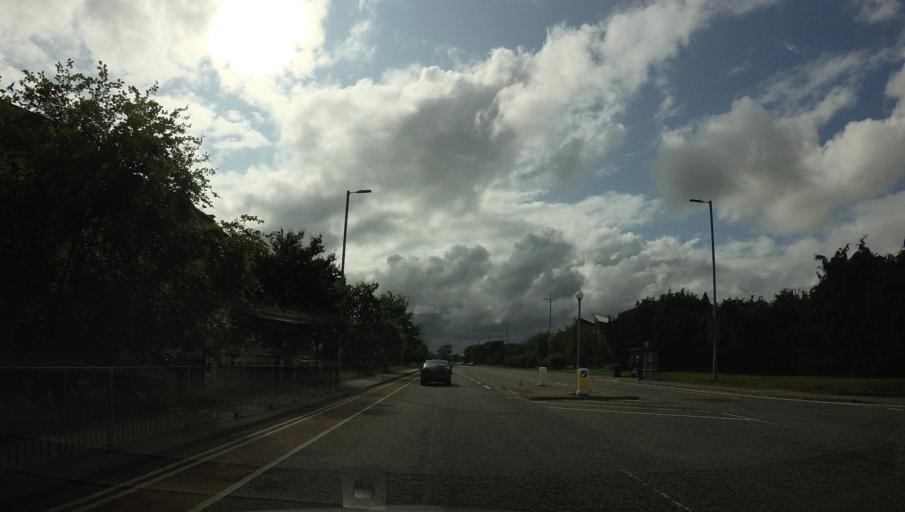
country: GB
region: Scotland
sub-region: Aberdeen City
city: Cults
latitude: 57.1507
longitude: -2.1765
